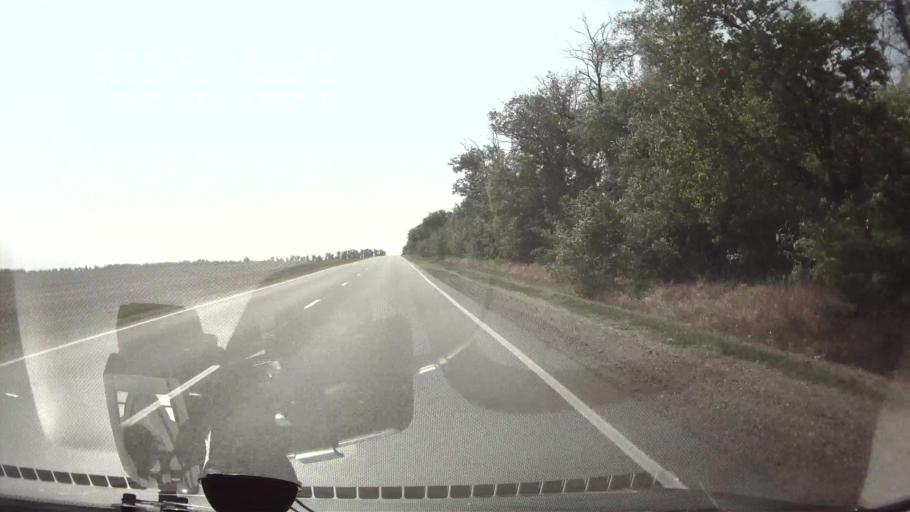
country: RU
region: Krasnodarskiy
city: Kavkazskaya
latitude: 45.5312
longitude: 40.6803
